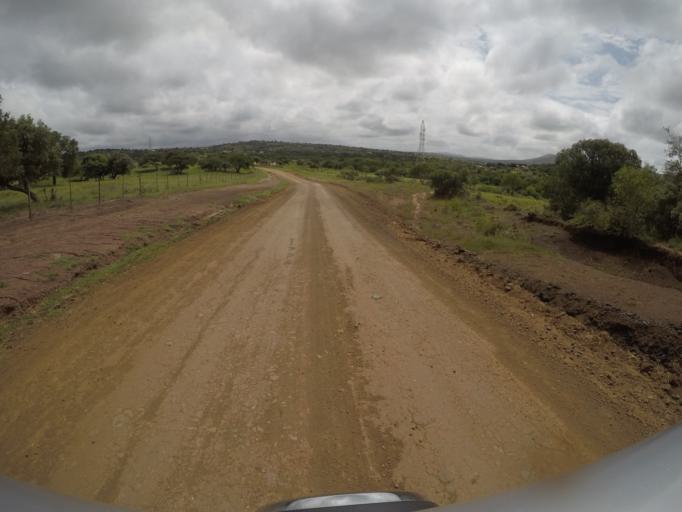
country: ZA
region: KwaZulu-Natal
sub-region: uThungulu District Municipality
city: Empangeni
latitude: -28.5940
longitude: 31.8407
